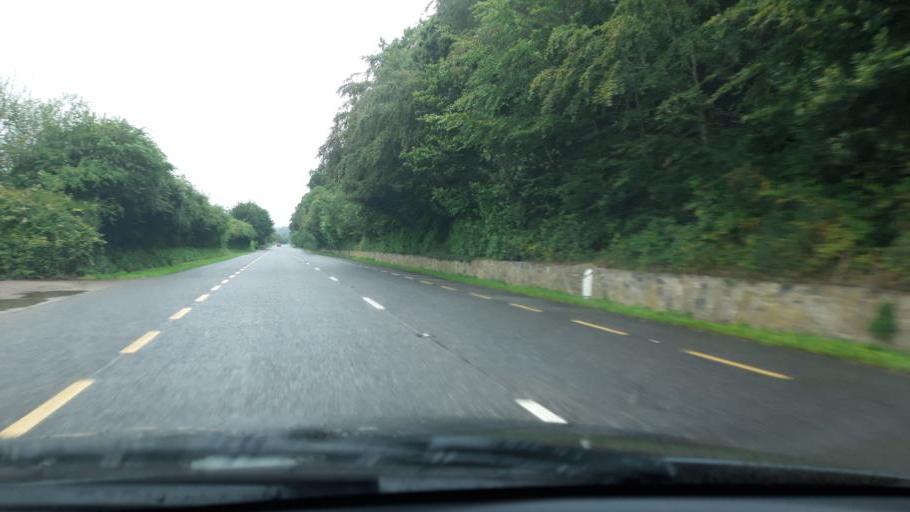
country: IE
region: Munster
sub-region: County Cork
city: Youghal
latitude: 52.1462
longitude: -7.8939
